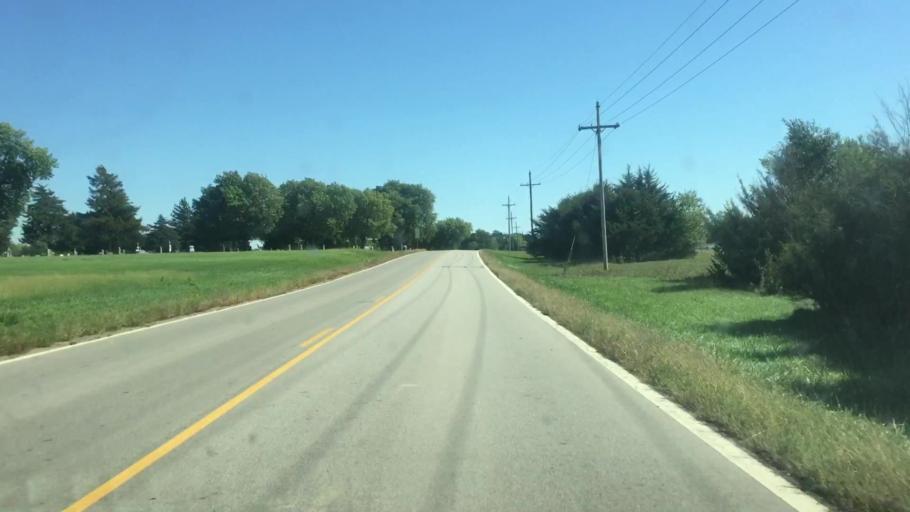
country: US
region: Kansas
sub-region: Jackson County
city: Holton
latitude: 39.6094
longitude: -95.7249
